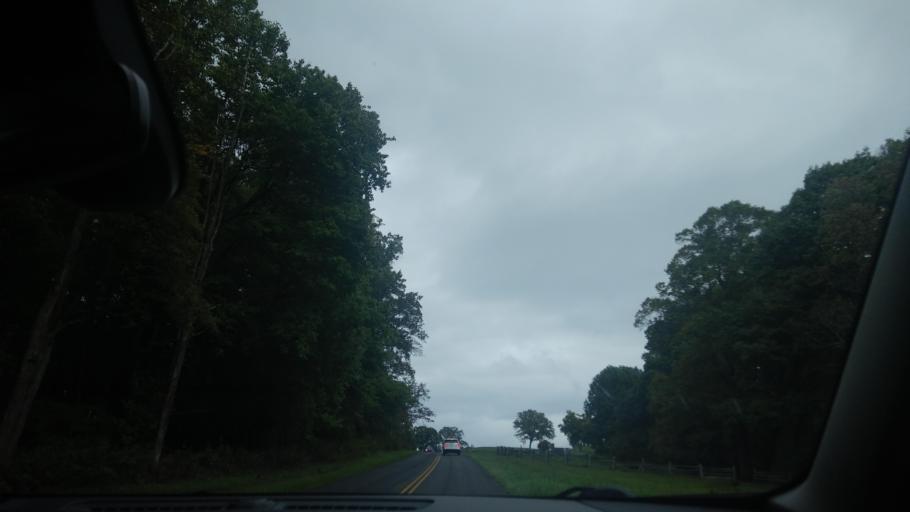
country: US
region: North Carolina
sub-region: Surry County
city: Flat Rock
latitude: 36.6439
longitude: -80.5320
